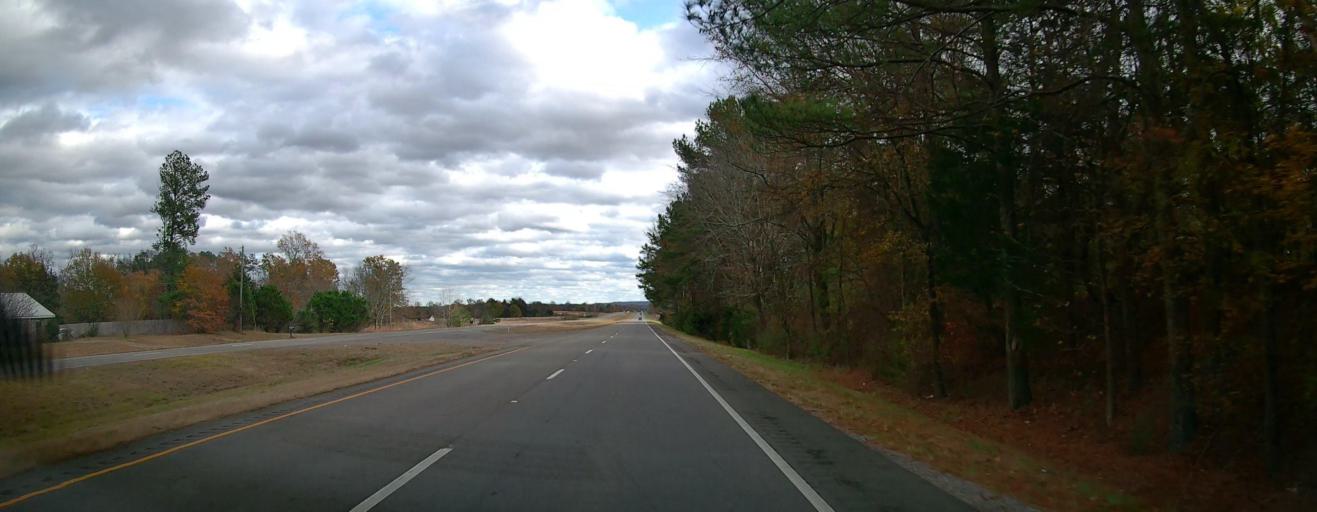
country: US
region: Alabama
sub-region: Morgan County
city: Danville
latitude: 34.3859
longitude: -87.1052
